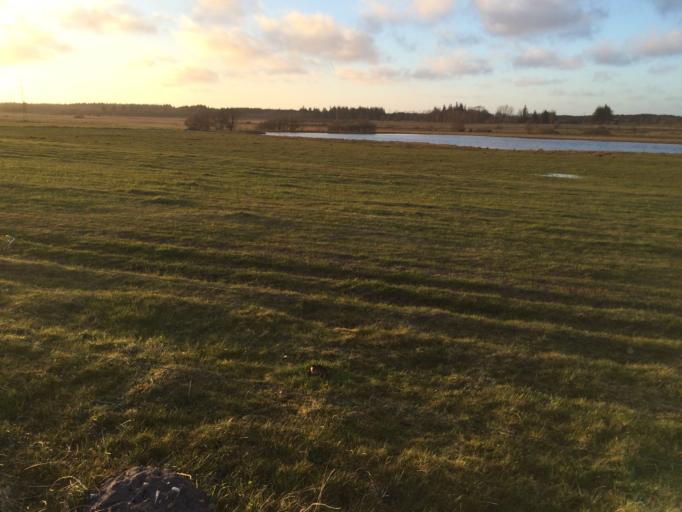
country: DK
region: Central Jutland
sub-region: Holstebro Kommune
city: Ulfborg
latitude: 56.2462
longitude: 8.4079
